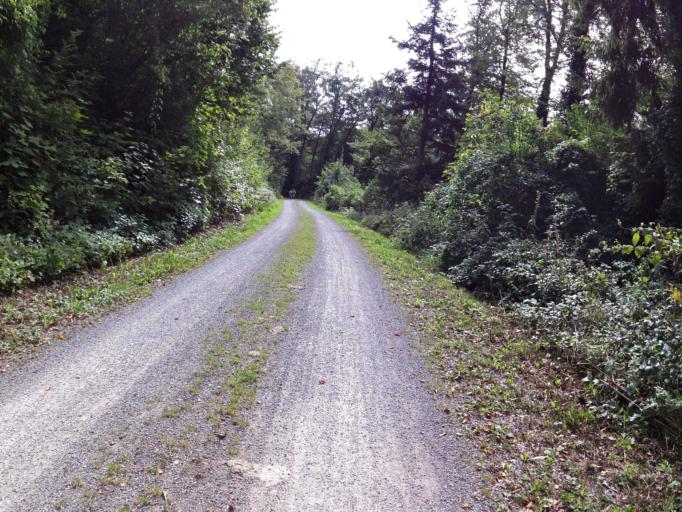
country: DE
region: Baden-Wuerttemberg
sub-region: Freiburg Region
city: Sulz am Neckar
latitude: 48.3381
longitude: 8.5929
